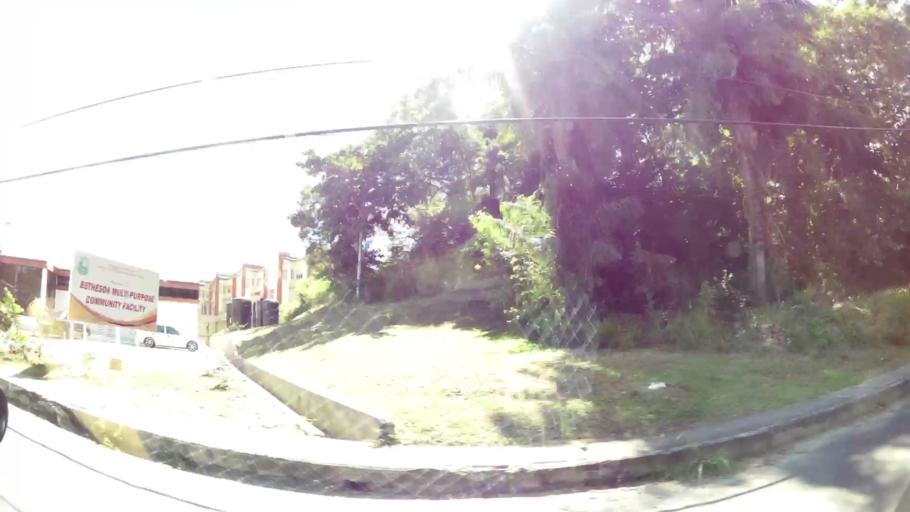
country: TT
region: Tobago
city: Scarborough
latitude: 11.2212
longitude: -60.7692
